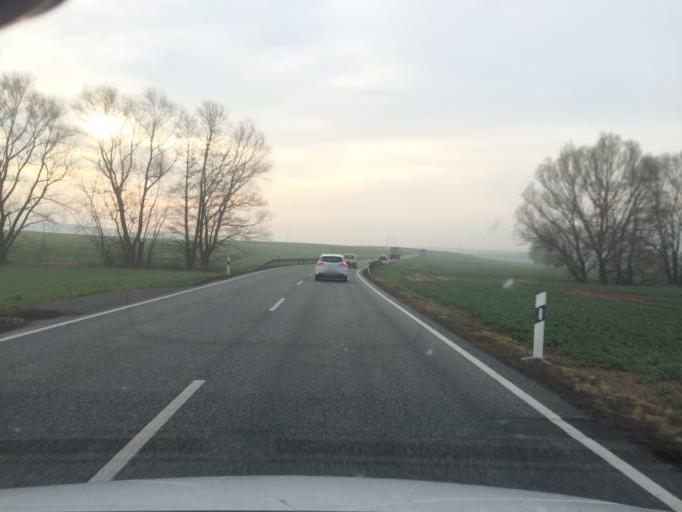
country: DE
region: Thuringia
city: Etzelsrode
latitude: 51.5316
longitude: 10.6181
